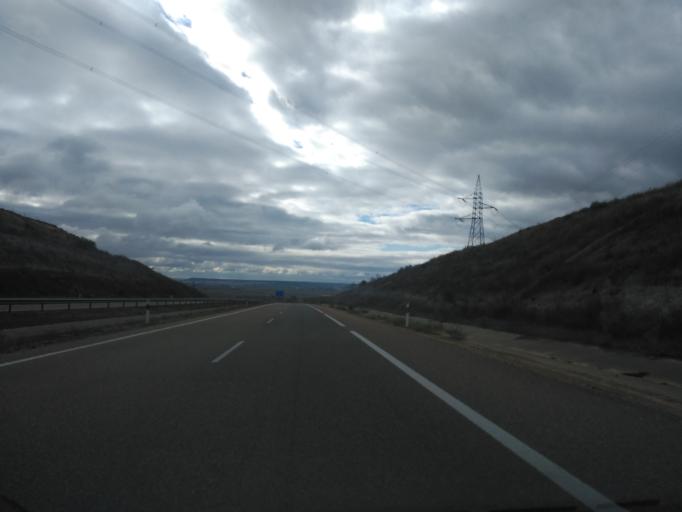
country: ES
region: Castille and Leon
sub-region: Provincia de Palencia
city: Fuentes de Valdepero
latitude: 42.0922
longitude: -4.4856
